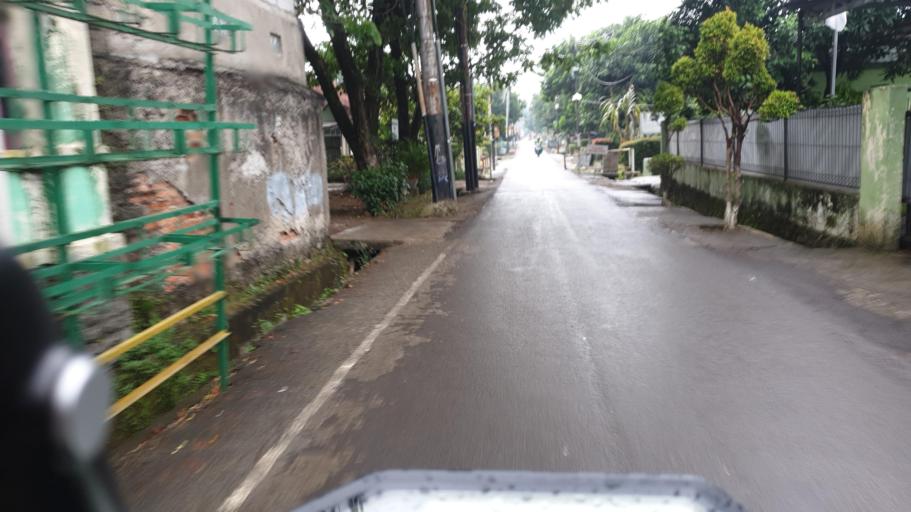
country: ID
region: West Java
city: Depok
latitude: -6.3450
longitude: 106.8309
